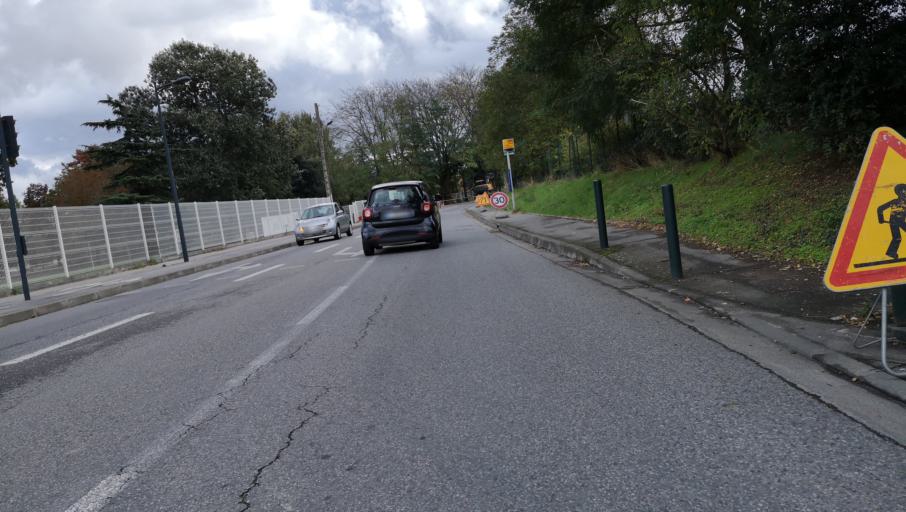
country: FR
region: Midi-Pyrenees
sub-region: Departement de la Haute-Garonne
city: Blagnac
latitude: 43.6110
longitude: 1.4040
